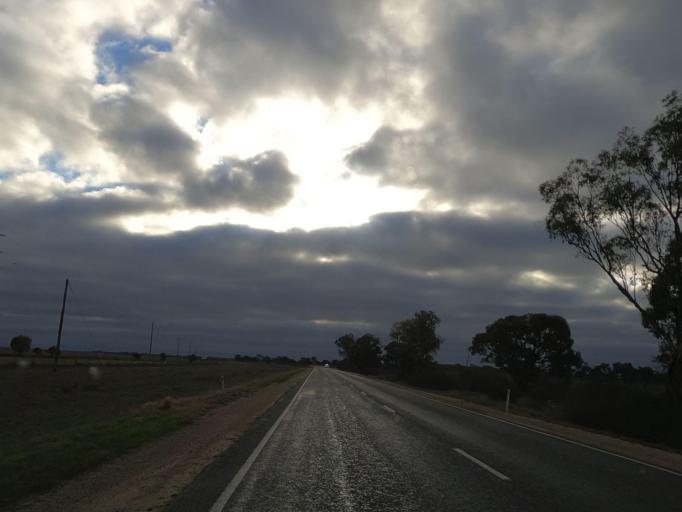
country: AU
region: Victoria
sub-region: Swan Hill
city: Swan Hill
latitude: -35.6544
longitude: 143.8488
